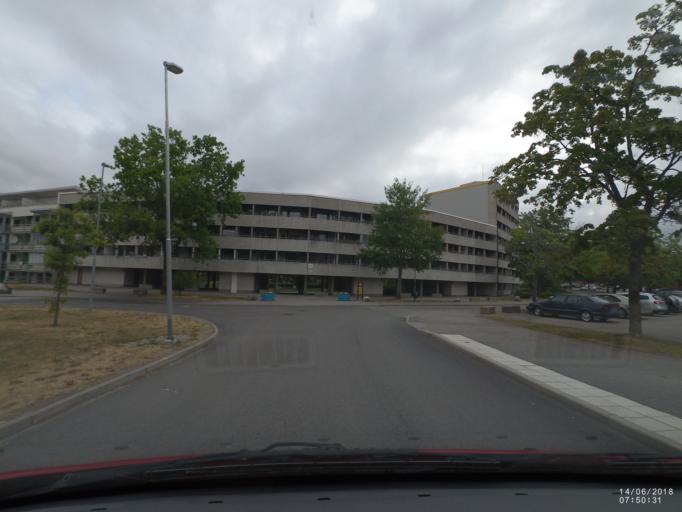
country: SE
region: Soedermanland
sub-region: Nykopings Kommun
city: Nykoping
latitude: 58.7647
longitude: 17.0218
